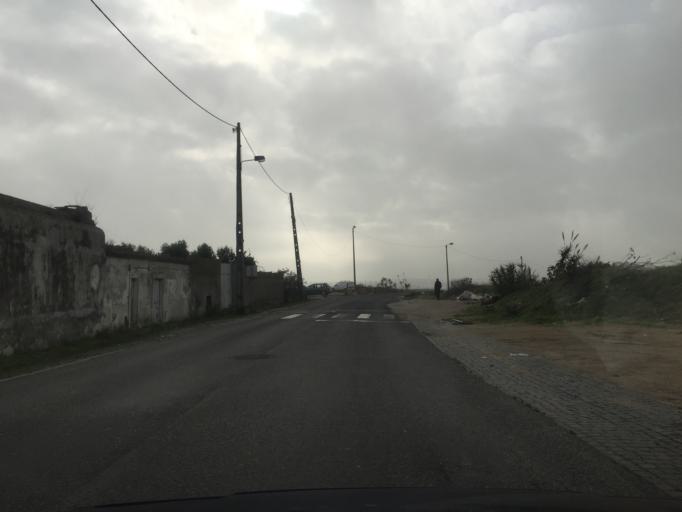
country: PT
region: Lisbon
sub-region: Loures
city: Camarate
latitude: 38.7809
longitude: -9.1410
